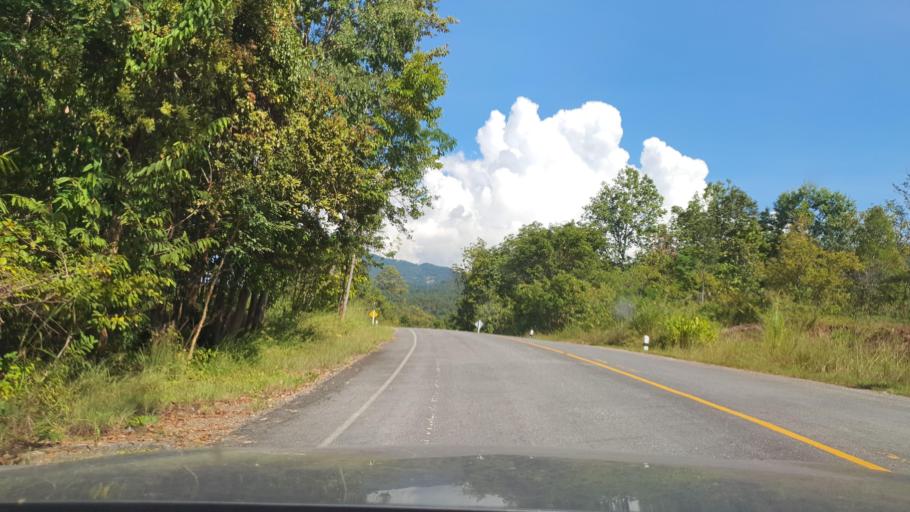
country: TH
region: Chiang Mai
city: Phrao
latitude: 19.3593
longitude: 99.2610
